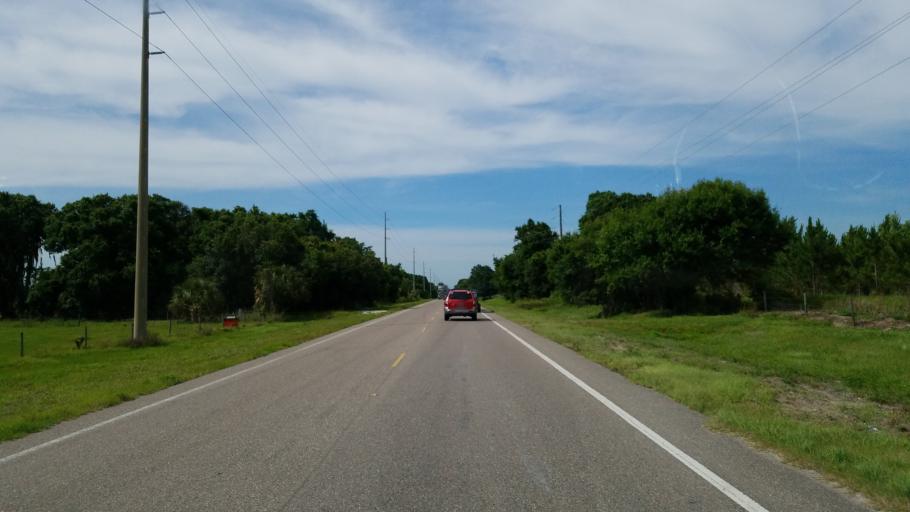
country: US
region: Florida
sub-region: Hillsborough County
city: Balm
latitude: 27.6743
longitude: -82.1462
